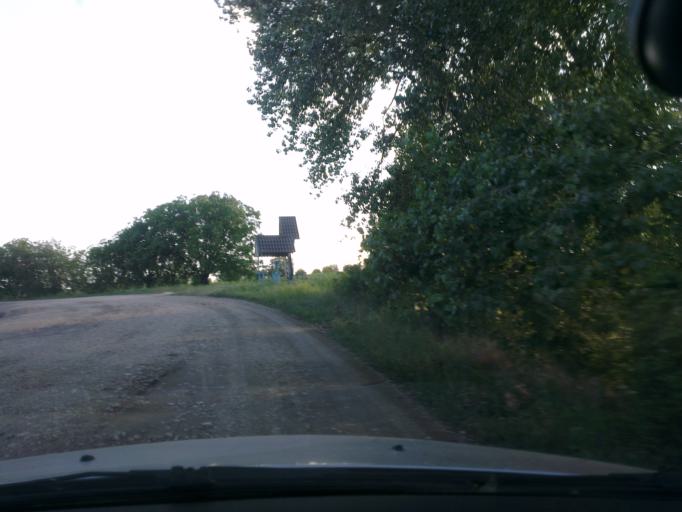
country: MD
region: Cantemir
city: Visniovca
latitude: 46.3468
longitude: 28.4032
